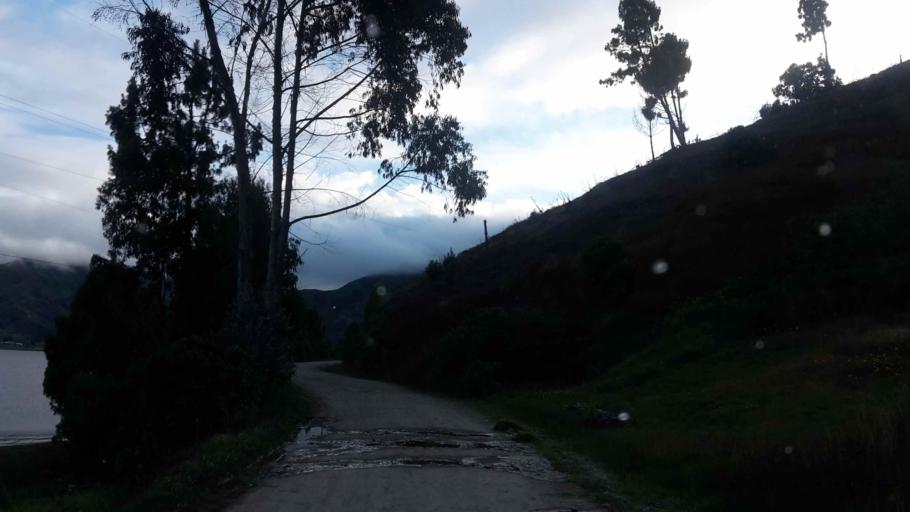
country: BO
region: Cochabamba
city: Colomi
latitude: -17.2764
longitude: -65.9096
